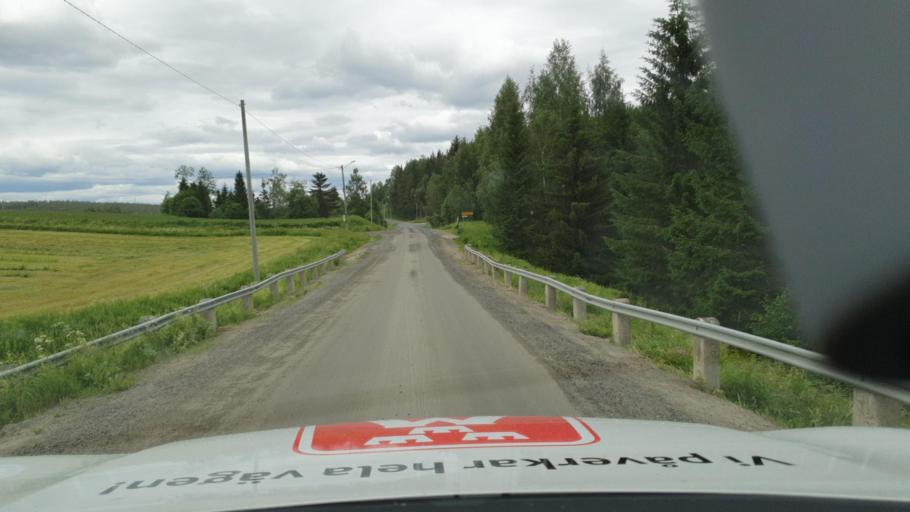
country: SE
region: Vaesterbotten
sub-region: Nordmalings Kommun
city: Nordmaling
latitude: 63.6713
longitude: 19.4385
